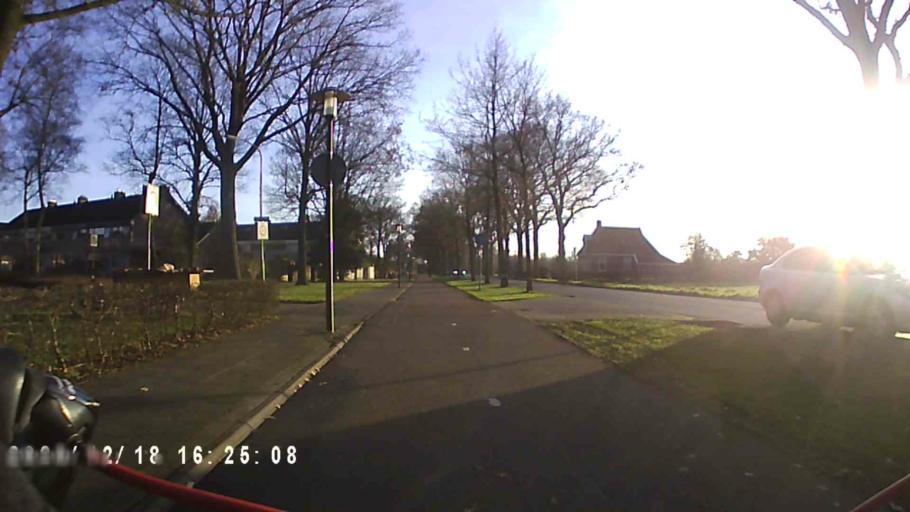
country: NL
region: Drenthe
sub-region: Gemeente Tynaarlo
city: Zuidlaren
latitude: 53.0849
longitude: 6.6949
